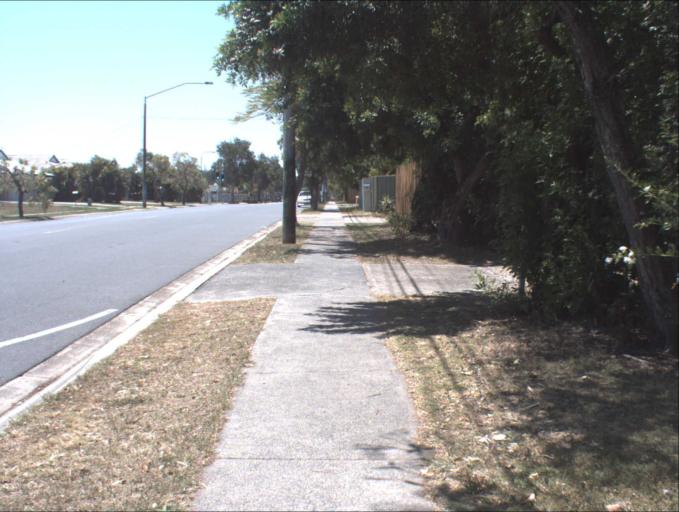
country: AU
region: Queensland
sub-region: Logan
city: Beenleigh
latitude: -27.6892
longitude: 153.1787
